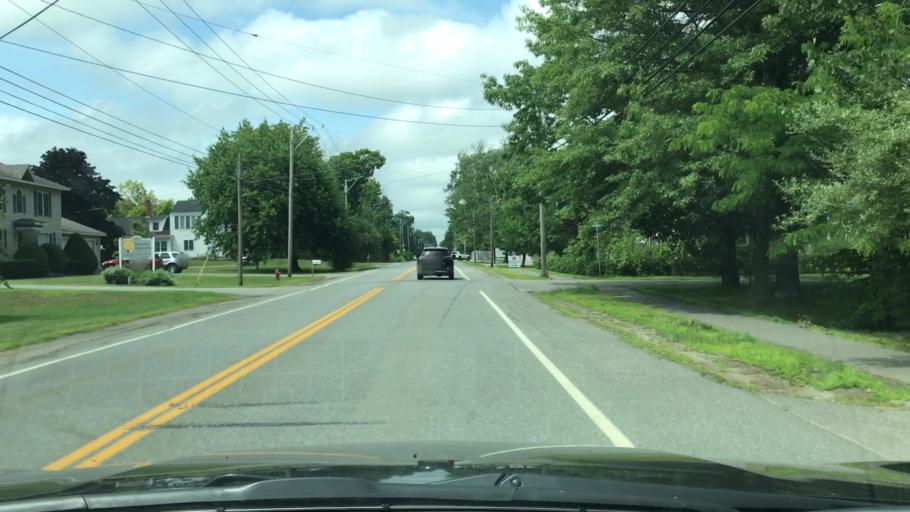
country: US
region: Maine
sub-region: Waldo County
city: Belfast
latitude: 44.4105
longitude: -68.9938
